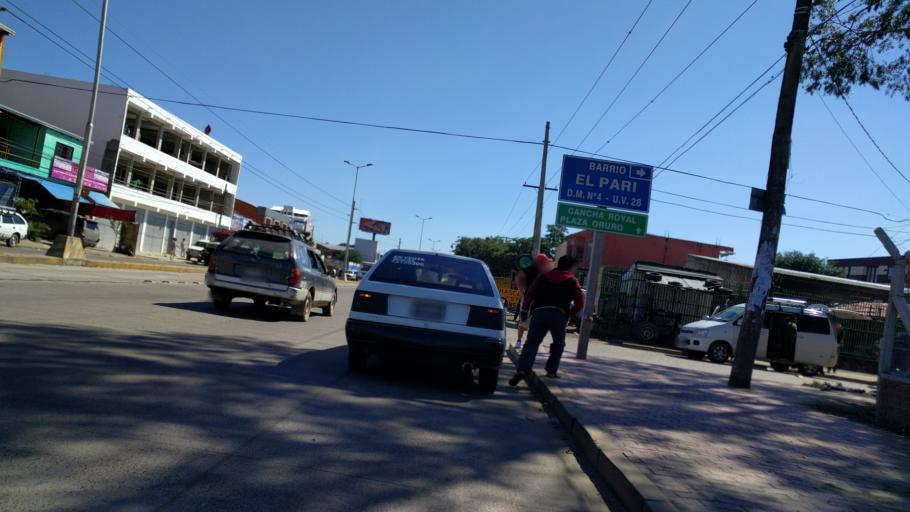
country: BO
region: Santa Cruz
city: Santa Cruz de la Sierra
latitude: -17.8058
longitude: -63.1976
